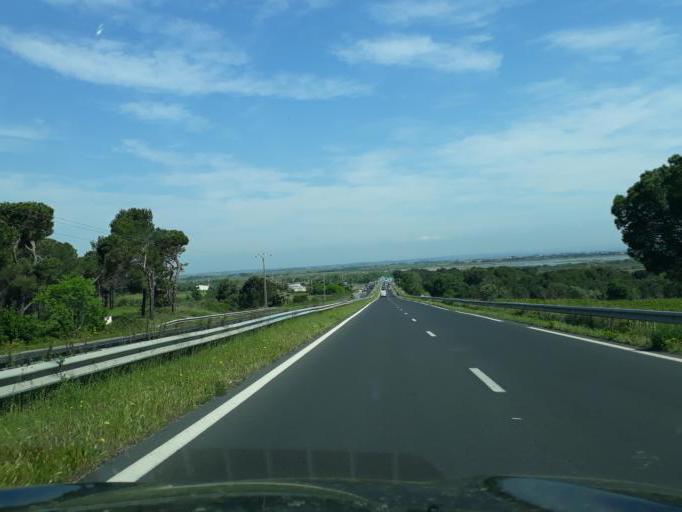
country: FR
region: Languedoc-Roussillon
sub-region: Departement de l'Herault
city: Le Cap d'Agde
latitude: 43.2995
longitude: 3.5076
